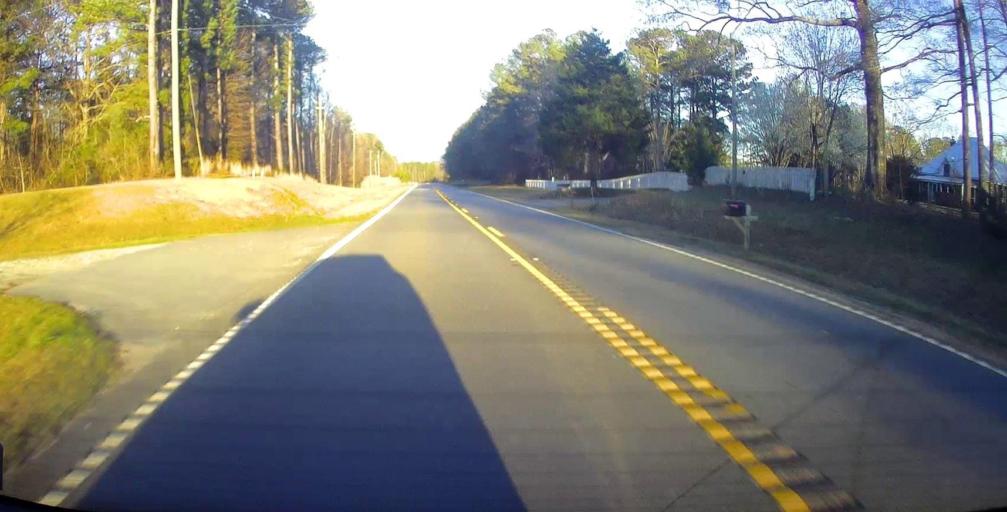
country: US
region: Georgia
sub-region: Harris County
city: Hamilton
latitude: 32.6727
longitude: -84.9314
